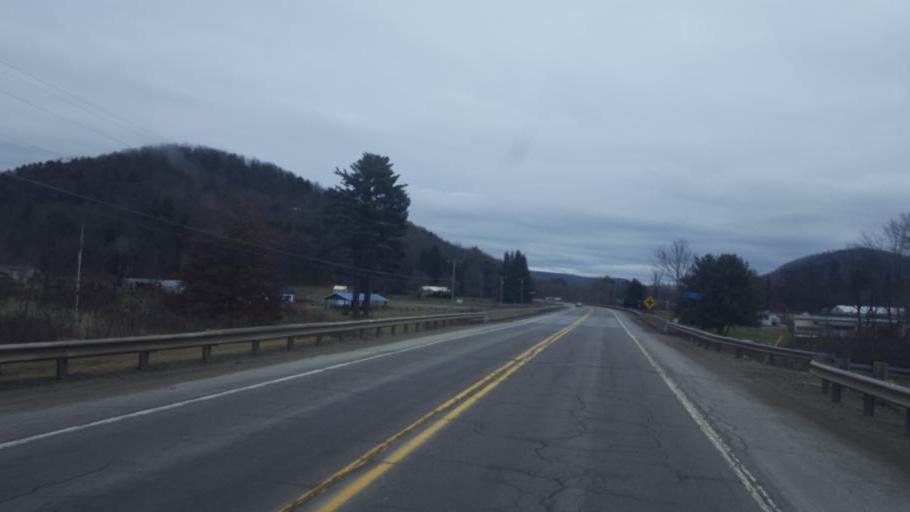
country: US
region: Pennsylvania
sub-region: McKean County
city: Port Allegany
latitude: 41.7850
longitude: -78.1641
